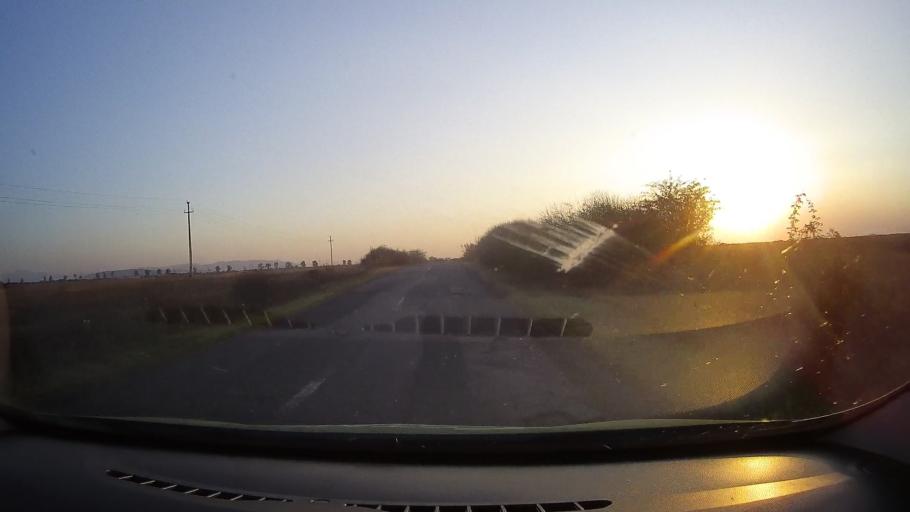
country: RO
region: Arad
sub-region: Comuna Seleus
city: Seleus
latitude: 46.4026
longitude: 21.7260
